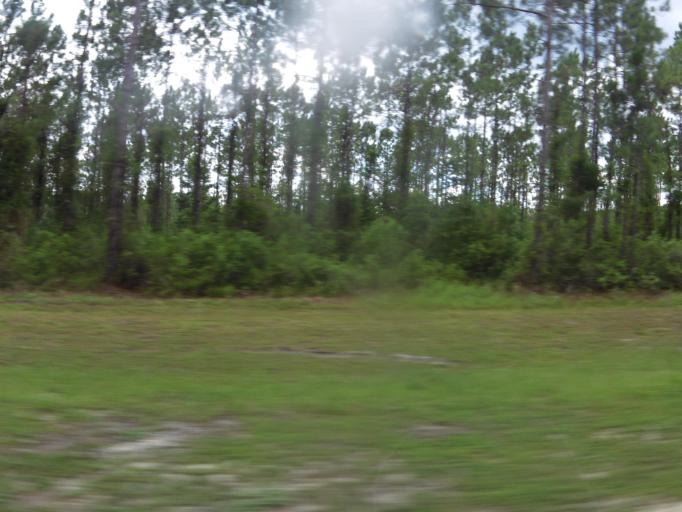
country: US
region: Georgia
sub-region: Camden County
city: Kingsland
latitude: 30.7695
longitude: -81.6491
